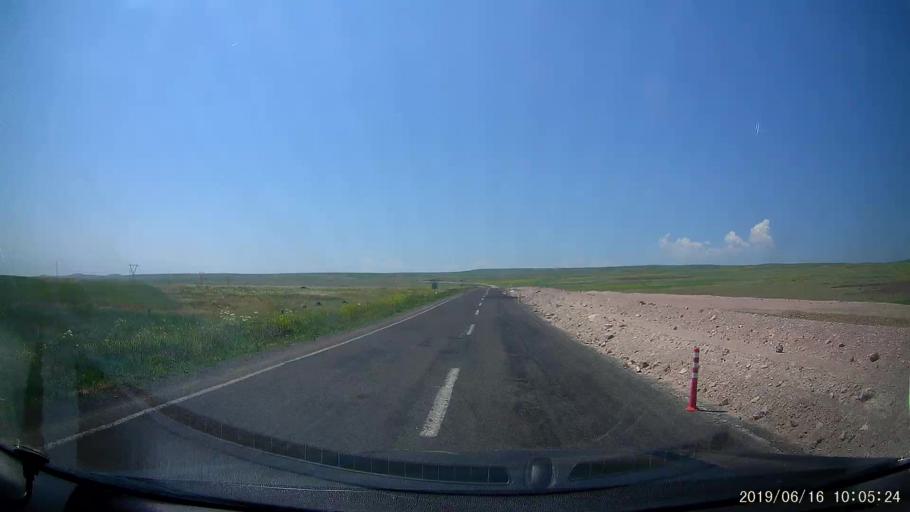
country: TR
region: Kars
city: Digor
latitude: 40.2709
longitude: 43.5384
